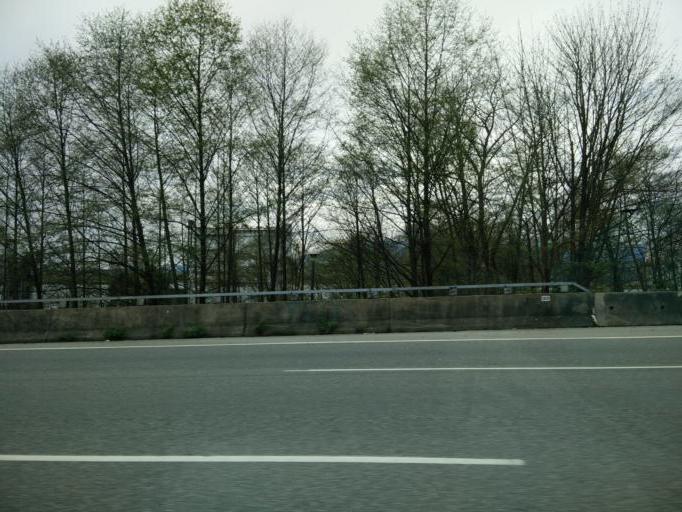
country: CA
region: British Columbia
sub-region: Fraser Valley Regional District
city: North Vancouver
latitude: 49.2902
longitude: -123.0273
